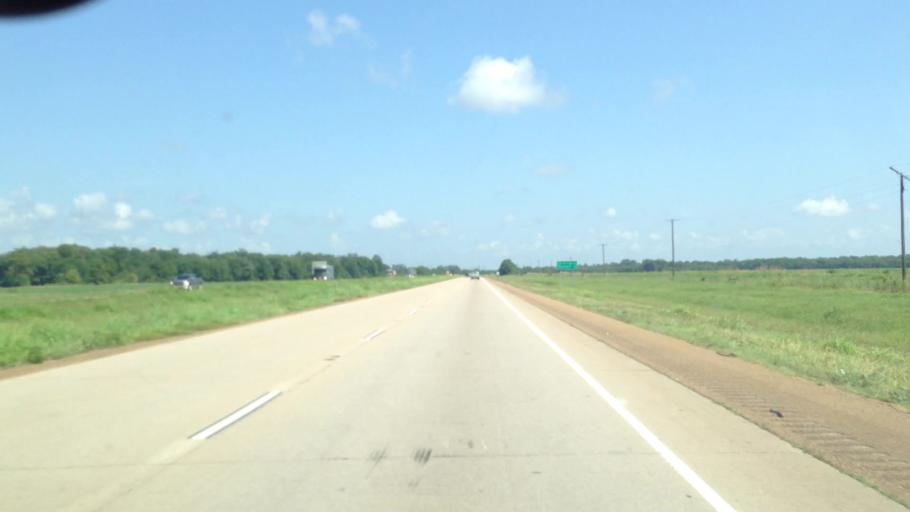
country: US
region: Louisiana
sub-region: Rapides Parish
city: Woodworth
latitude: 31.1765
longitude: -92.4664
